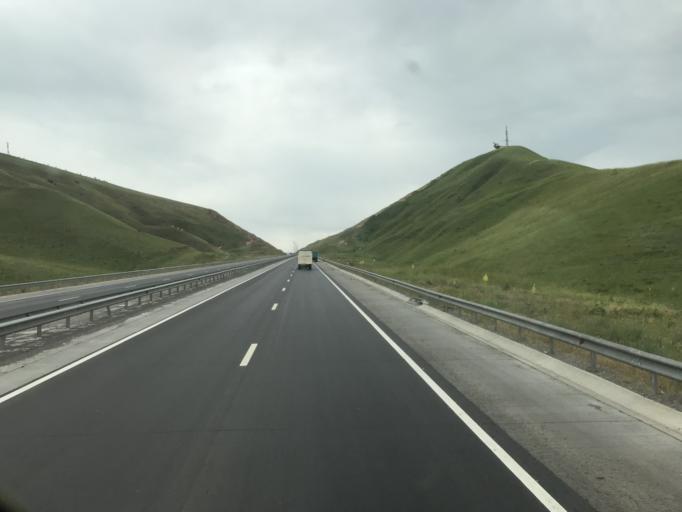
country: KZ
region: Ongtustik Qazaqstan
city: Qazyqurt
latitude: 42.0053
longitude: 69.4739
